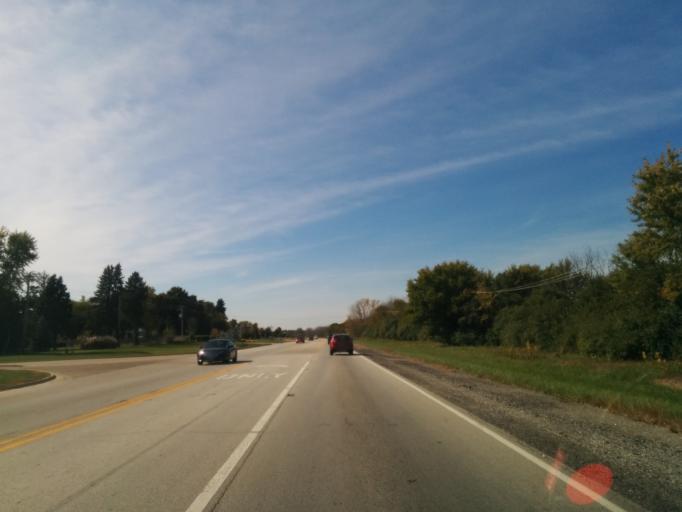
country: US
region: Illinois
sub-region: DuPage County
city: Warrenville
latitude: 41.8206
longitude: -88.2205
